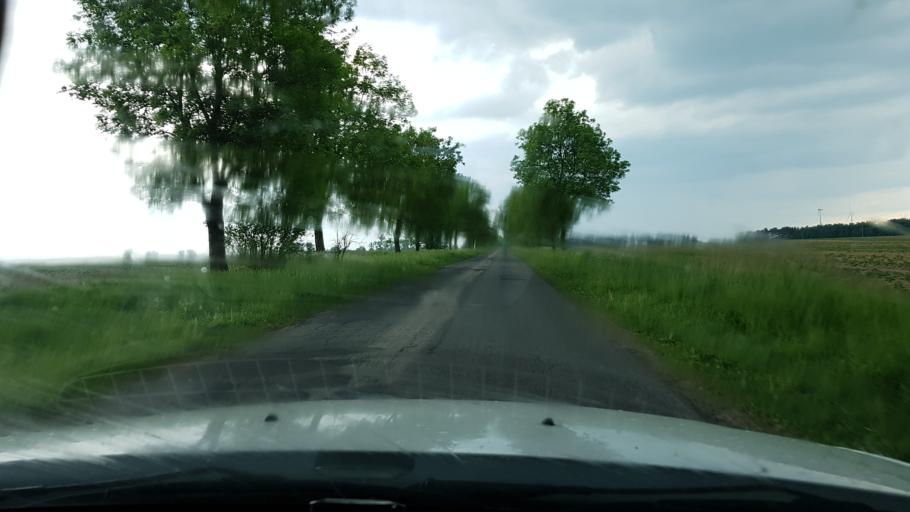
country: PL
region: West Pomeranian Voivodeship
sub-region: Powiat stargardzki
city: Marianowo
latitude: 53.3337
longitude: 15.1914
